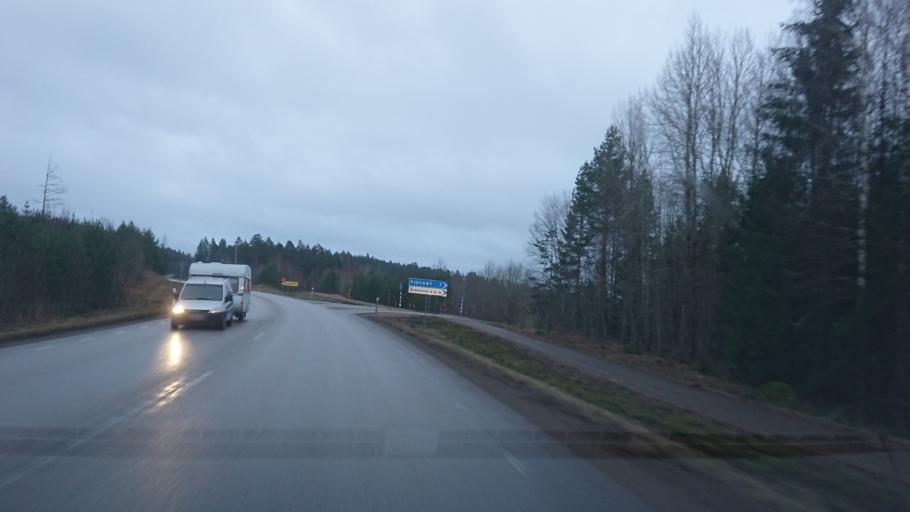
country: SE
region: Uppsala
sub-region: Osthammars Kommun
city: Bjorklinge
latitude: 60.0111
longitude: 17.5903
